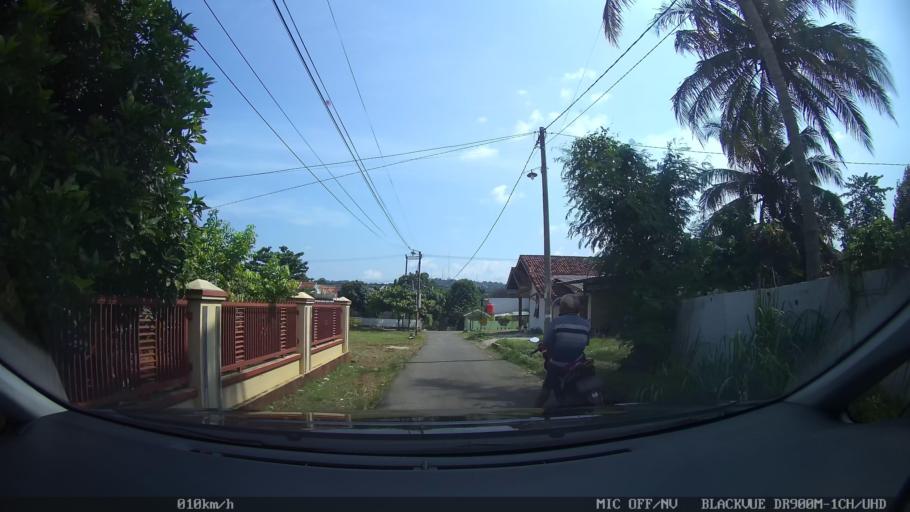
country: ID
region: Lampung
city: Kedaton
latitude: -5.4019
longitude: 105.2380
